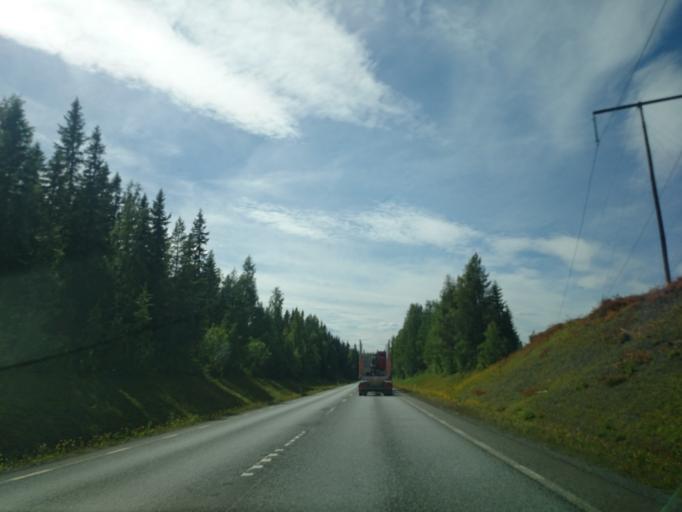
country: SE
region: Jaemtland
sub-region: Krokoms Kommun
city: Krokom
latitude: 63.3212
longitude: 14.2319
